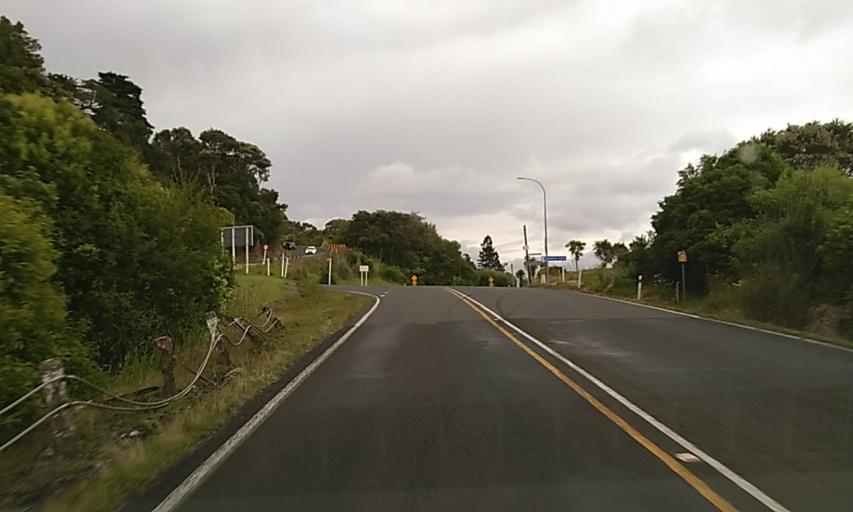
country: NZ
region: Auckland
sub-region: Auckland
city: Pukekohe East
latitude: -37.3000
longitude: 174.9448
